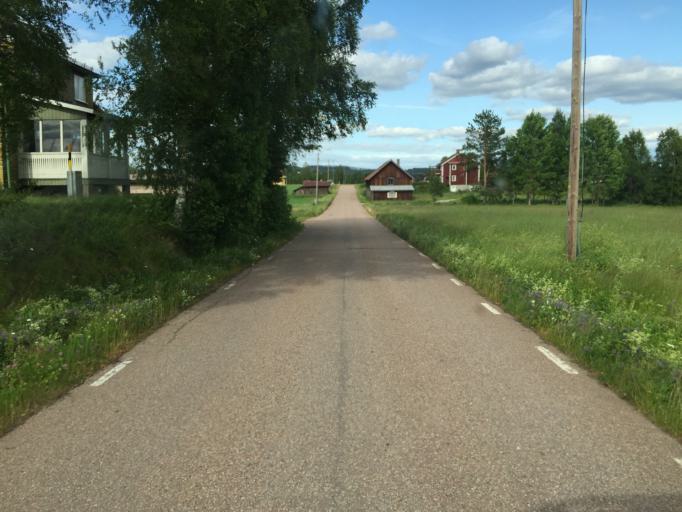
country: SE
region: Dalarna
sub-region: Alvdalens Kommun
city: AElvdalen
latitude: 60.9497
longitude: 13.8983
